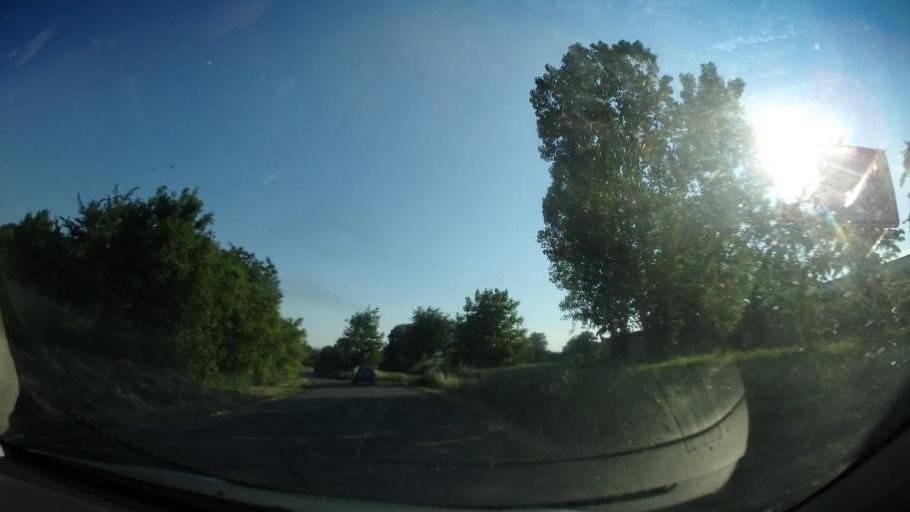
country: CZ
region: Olomoucky
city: Nemcice nad Hanou
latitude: 49.3444
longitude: 17.2512
